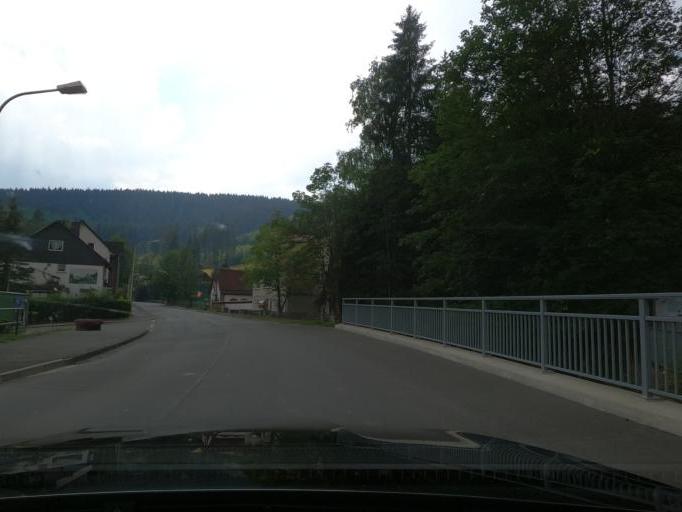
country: DE
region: Lower Saxony
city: Wildemann
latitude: 51.8229
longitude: 10.2725
